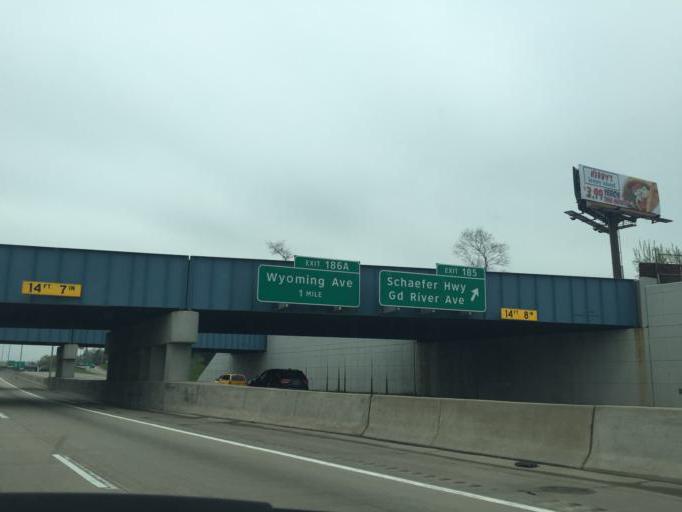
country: US
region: Michigan
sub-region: Wayne County
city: Dearborn
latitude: 42.3819
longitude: -83.1838
